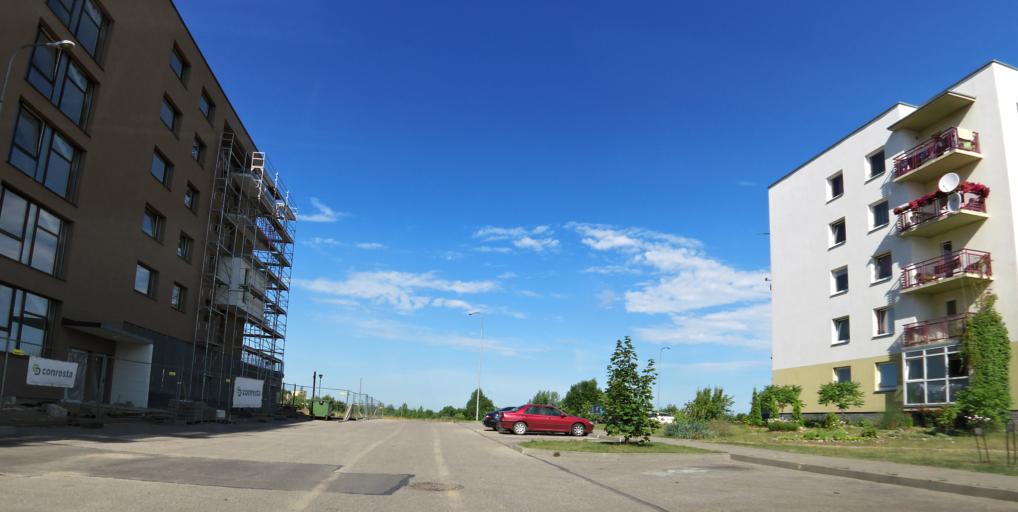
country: LT
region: Vilnius County
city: Pilaite
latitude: 54.7051
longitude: 25.1734
